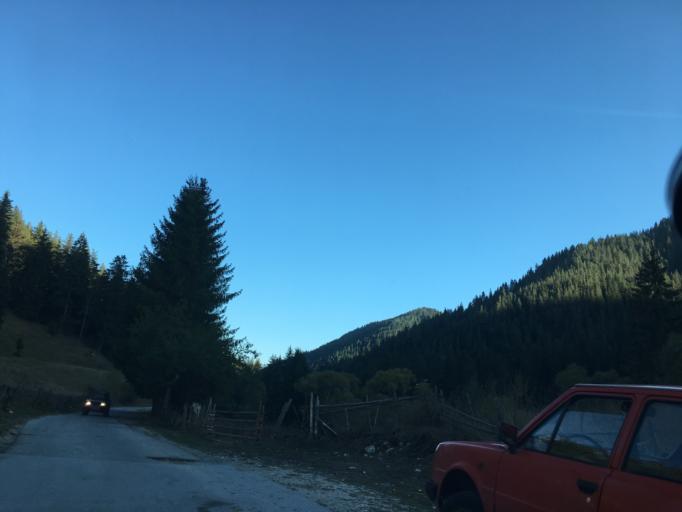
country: BG
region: Smolyan
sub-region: Obshtina Borino
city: Borino
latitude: 41.5897
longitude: 24.3838
